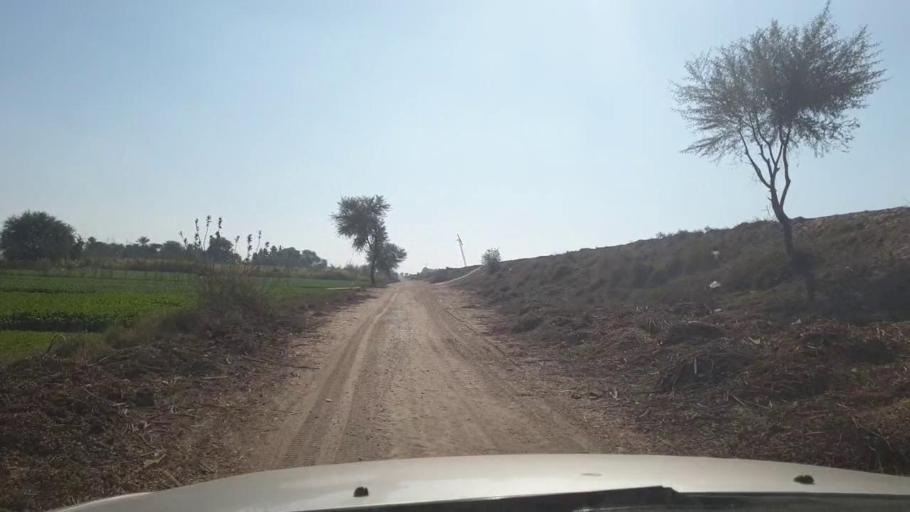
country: PK
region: Sindh
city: Ghotki
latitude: 28.0275
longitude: 69.2104
